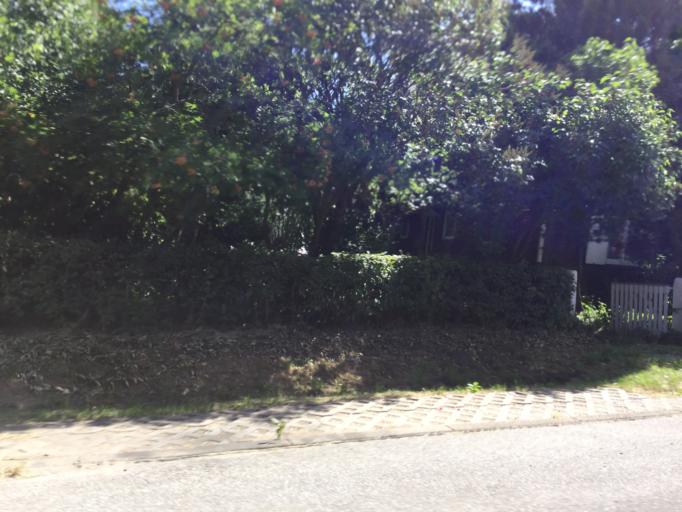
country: DE
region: Hamburg
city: Farmsen-Berne
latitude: 53.6283
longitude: 10.1276
